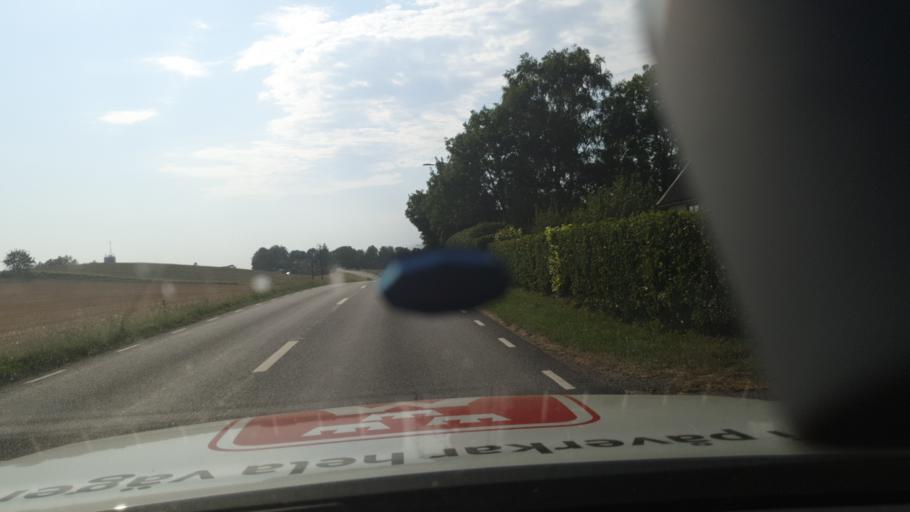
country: SE
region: Skane
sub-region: Svedala Kommun
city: Svedala
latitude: 55.4539
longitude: 13.2238
